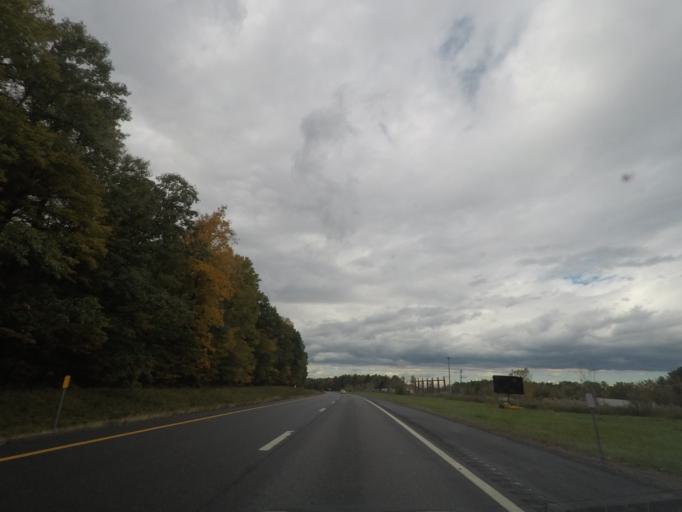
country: US
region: New York
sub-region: Rensselaer County
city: Castleton-on-Hudson
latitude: 42.4920
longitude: -73.7074
